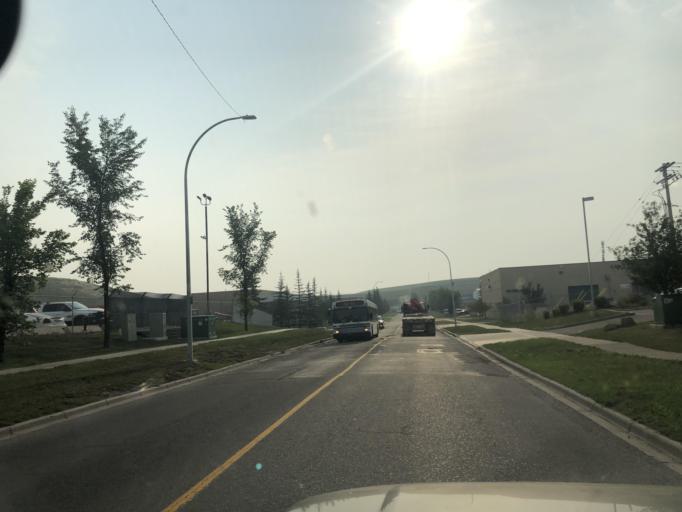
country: CA
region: Alberta
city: Calgary
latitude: 50.9568
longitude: -113.9995
